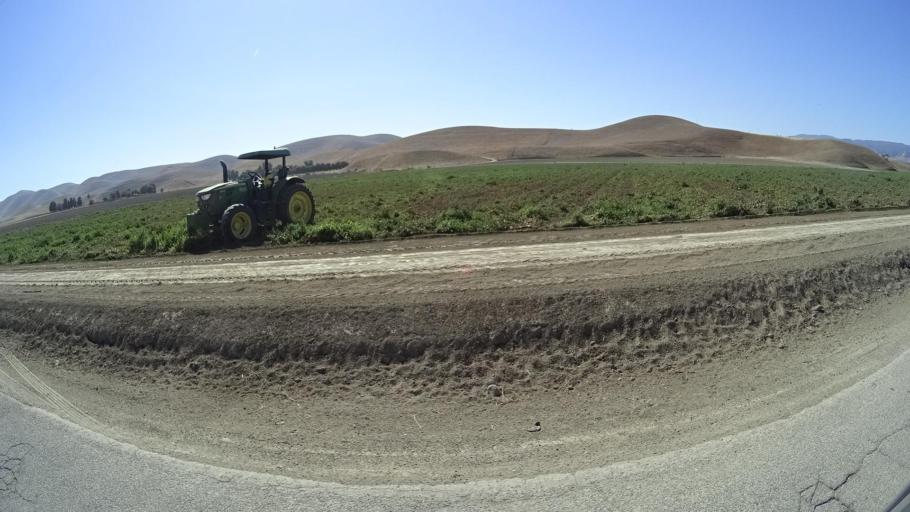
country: US
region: California
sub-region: Monterey County
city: King City
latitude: 36.0779
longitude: -120.9234
